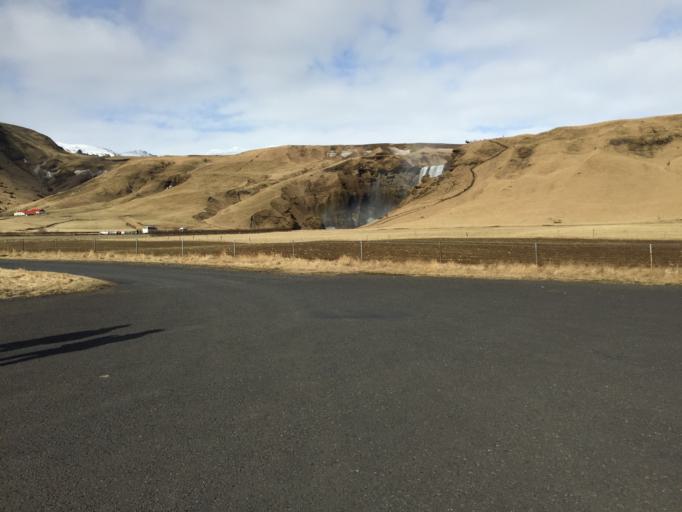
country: IS
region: South
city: Vestmannaeyjar
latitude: 63.5270
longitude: -19.5097
